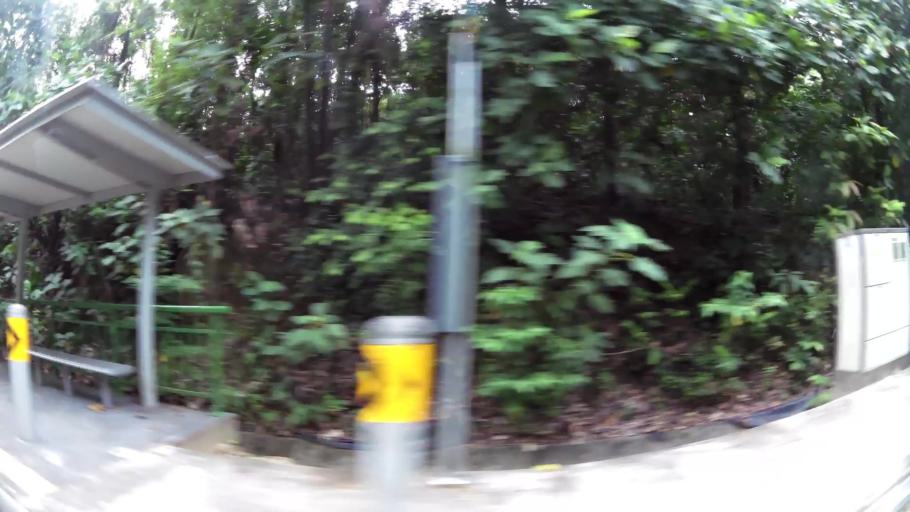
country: SG
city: Singapore
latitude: 1.2891
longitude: 103.7841
